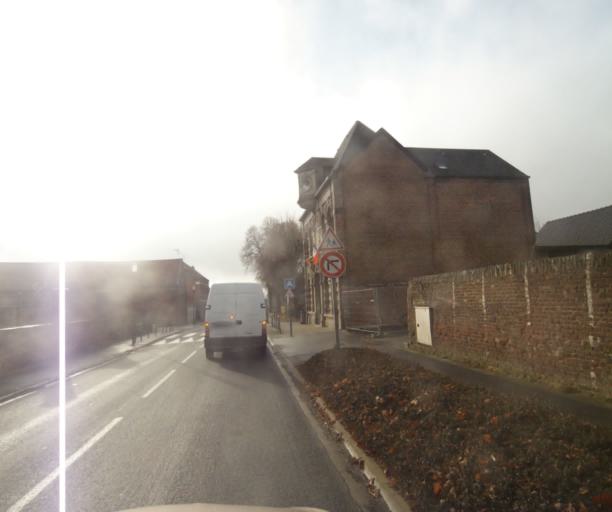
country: FR
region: Nord-Pas-de-Calais
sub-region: Departement du Nord
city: Vendegies-sur-Ecaillon
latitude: 50.2885
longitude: 3.5137
